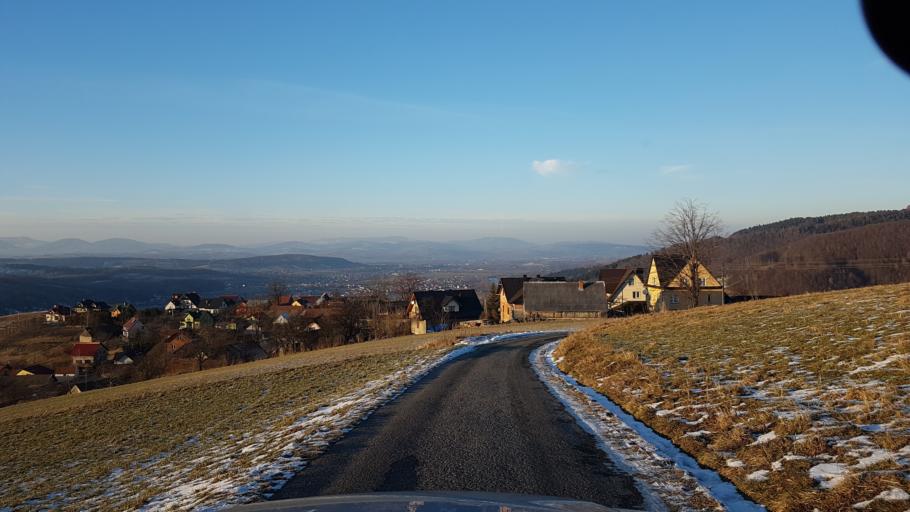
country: PL
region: Lesser Poland Voivodeship
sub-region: Powiat nowosadecki
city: Rytro
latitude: 49.5099
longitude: 20.6718
